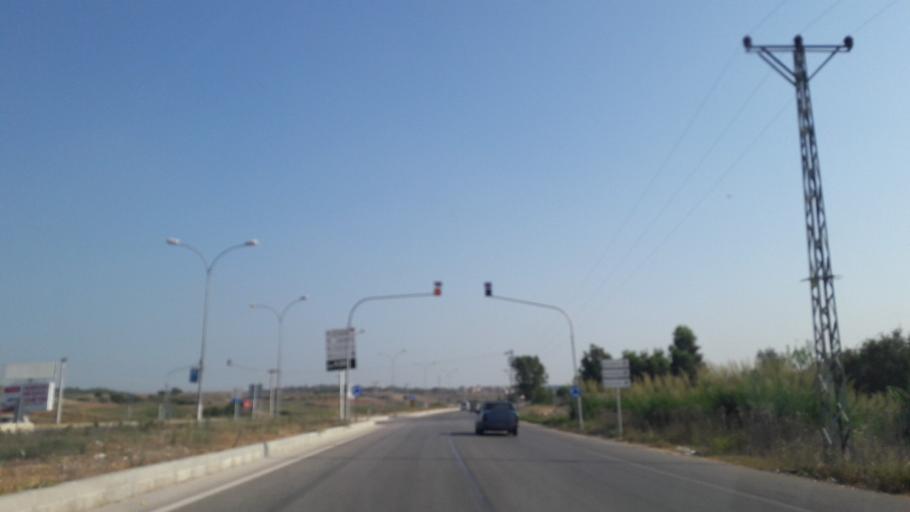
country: TR
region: Adana
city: Yuregir
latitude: 37.0612
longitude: 35.4444
